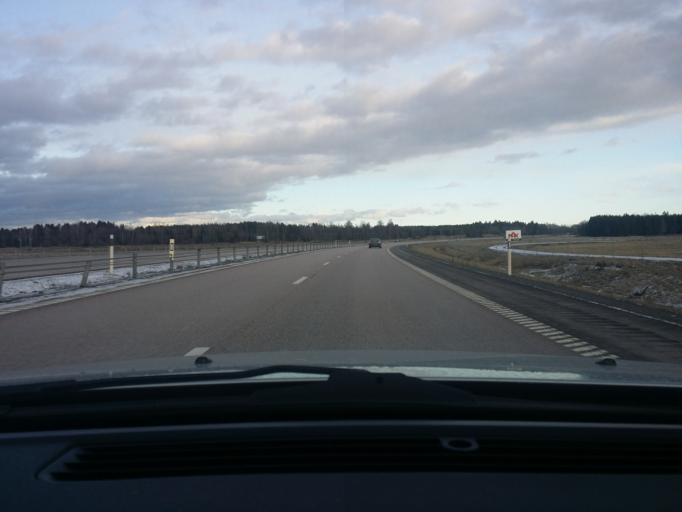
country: SE
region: Uppsala
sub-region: Enkopings Kommun
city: Hummelsta
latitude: 59.6475
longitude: 16.9758
